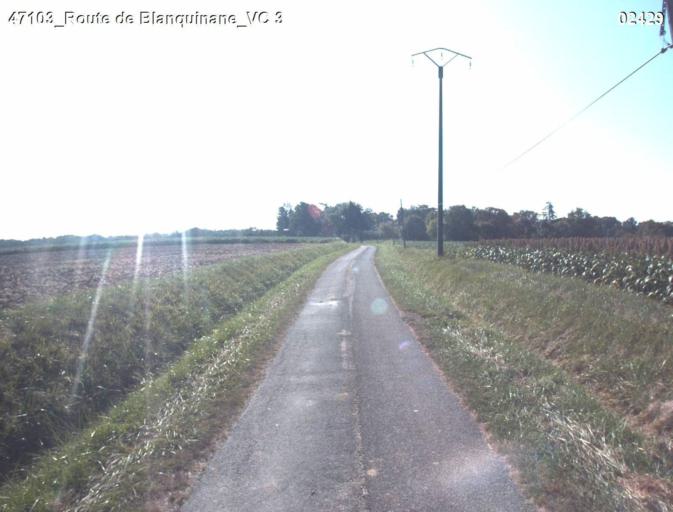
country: FR
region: Aquitaine
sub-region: Departement du Lot-et-Garonne
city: Nerac
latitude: 44.0877
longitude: 0.3369
